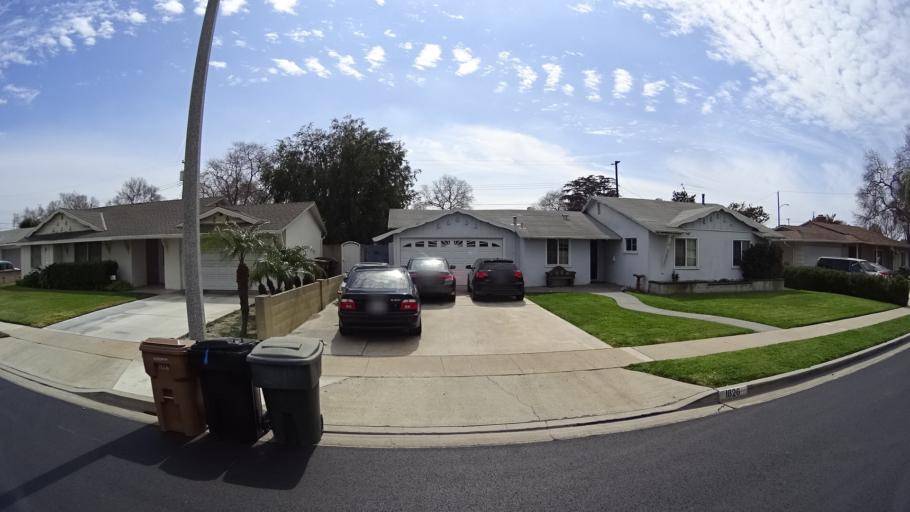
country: US
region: California
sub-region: Orange County
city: Garden Grove
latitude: 33.8098
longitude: -117.9470
